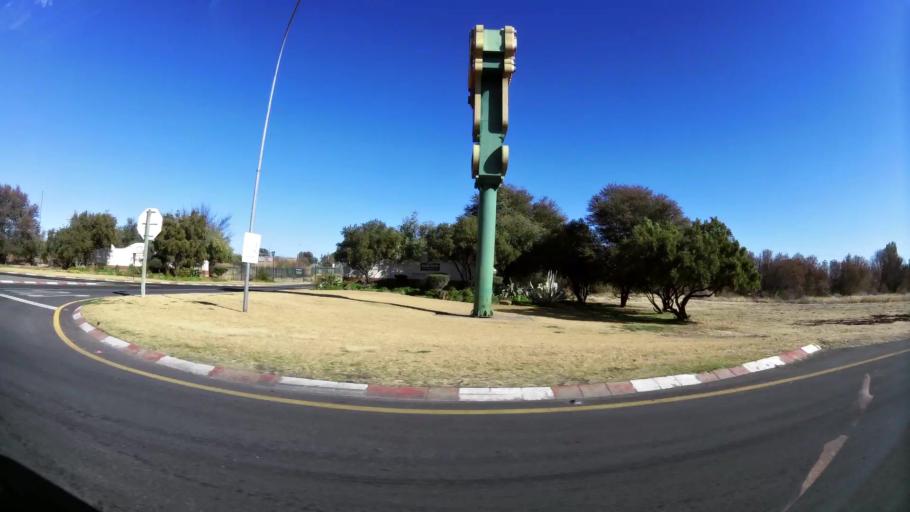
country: ZA
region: Northern Cape
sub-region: Frances Baard District Municipality
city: Kimberley
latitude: -28.6911
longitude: 24.7783
